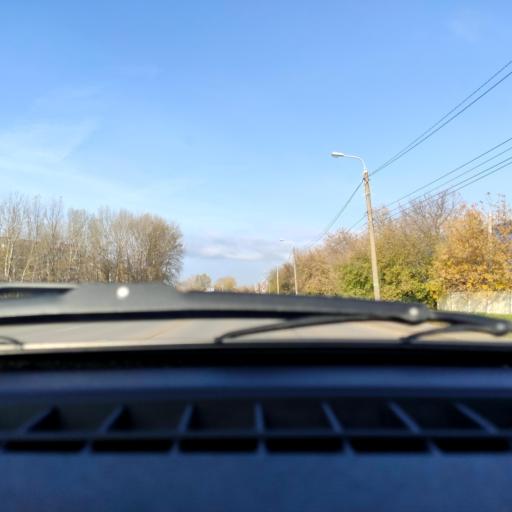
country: RU
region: Bashkortostan
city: Iglino
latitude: 54.7677
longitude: 56.2337
